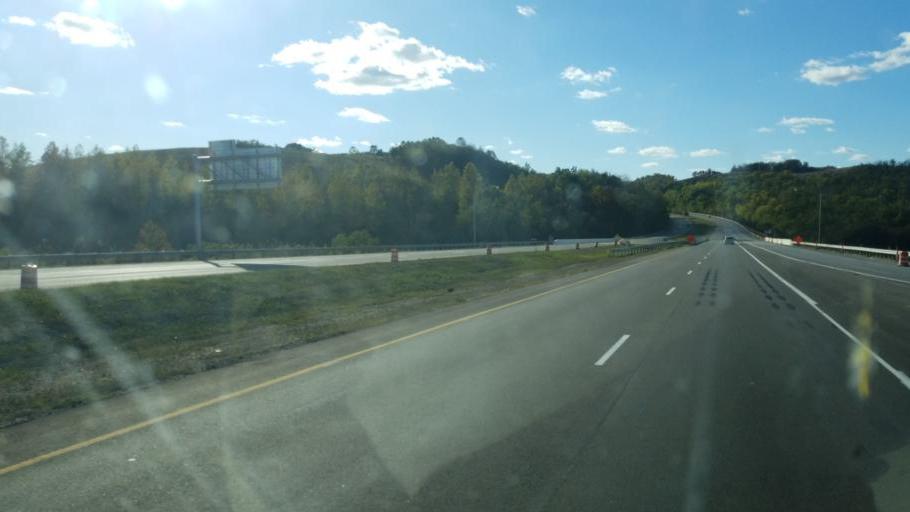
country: US
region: Ohio
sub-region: Belmont County
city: Bethesda
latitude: 40.0575
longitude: -81.1175
